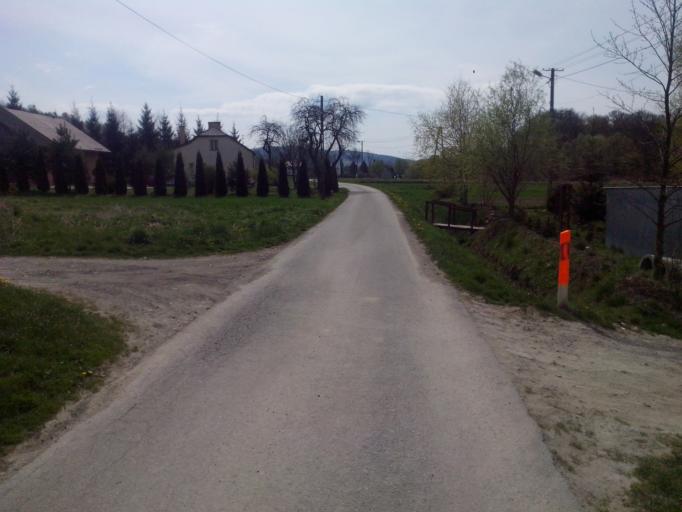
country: PL
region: Subcarpathian Voivodeship
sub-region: Powiat strzyzowski
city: Jawornik
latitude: 49.8214
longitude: 21.8420
